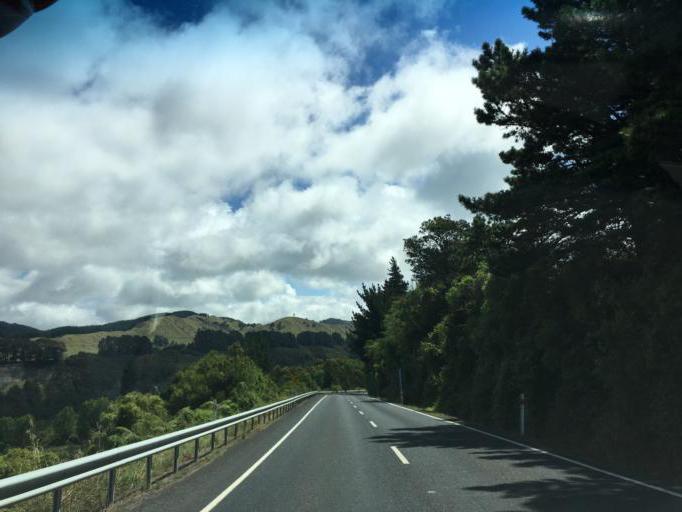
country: NZ
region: Hawke's Bay
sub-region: Wairoa District
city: Wairoa
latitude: -39.0744
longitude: 177.1420
